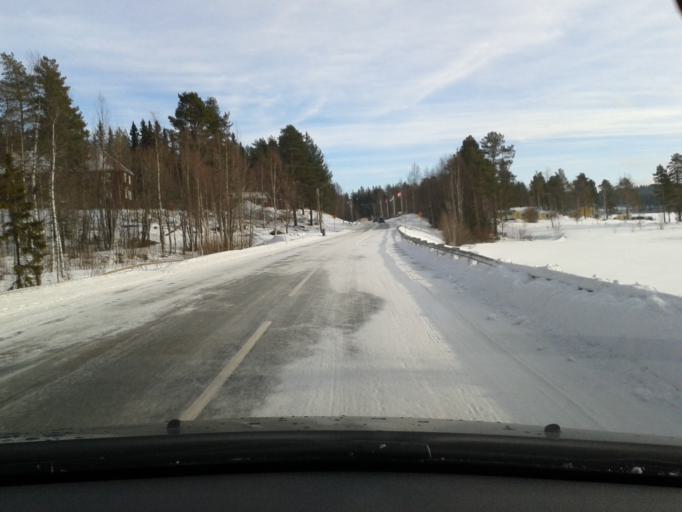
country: SE
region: Vaesterbotten
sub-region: Vilhelmina Kommun
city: Vilhelmina
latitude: 64.6503
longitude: 16.5857
